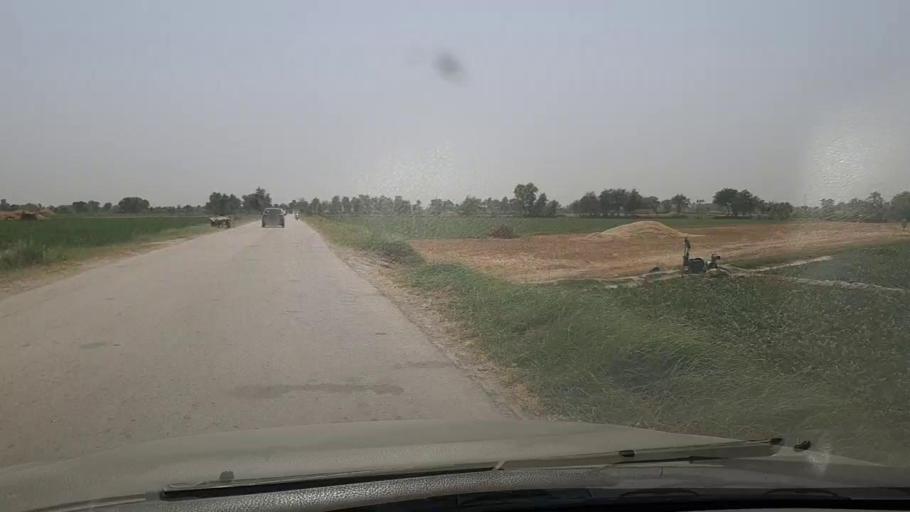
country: PK
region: Sindh
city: Kambar
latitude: 27.6241
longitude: 68.0241
